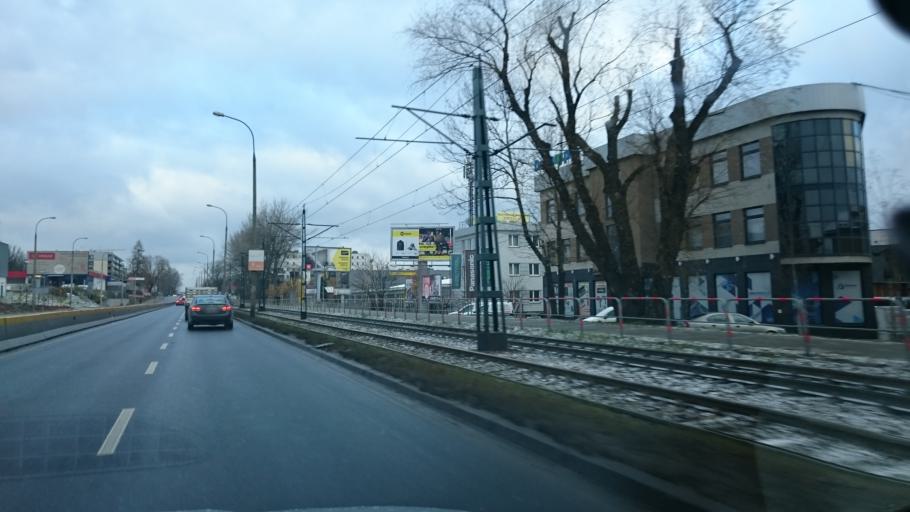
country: PL
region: Lesser Poland Voivodeship
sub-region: Krakow
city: Krakow
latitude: 50.0341
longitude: 19.9695
